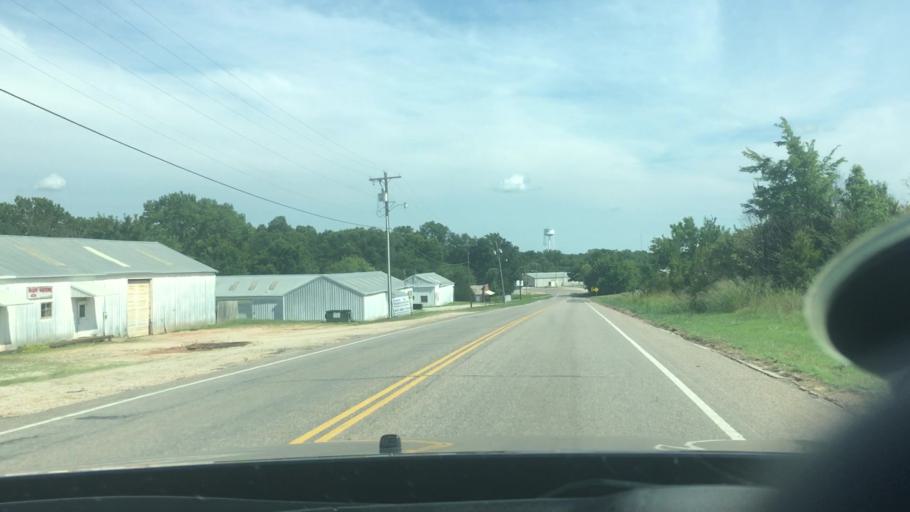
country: US
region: Oklahoma
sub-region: Seminole County
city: Seminole
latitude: 35.2275
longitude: -96.6821
